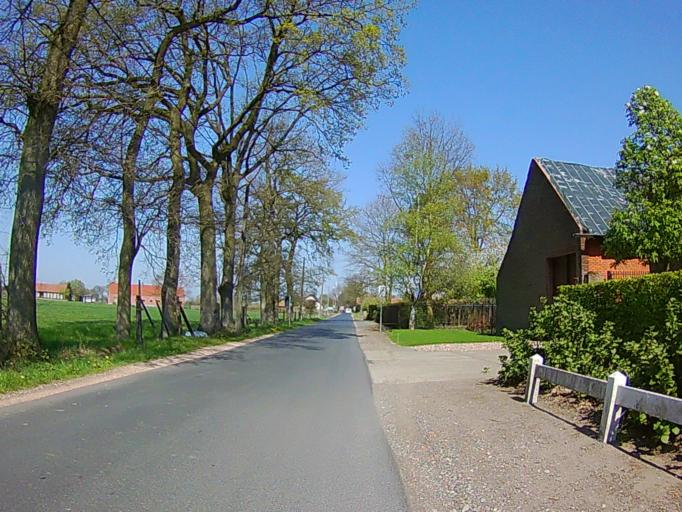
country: BE
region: Flanders
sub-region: Provincie Antwerpen
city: Brecht
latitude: 51.3538
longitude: 4.6646
